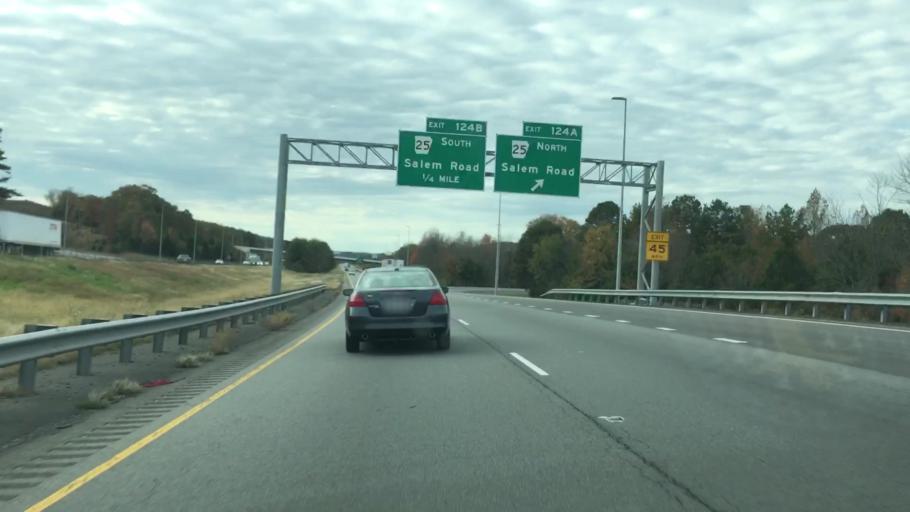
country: US
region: Arkansas
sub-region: Faulkner County
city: Conway
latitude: 35.1188
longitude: -92.4535
